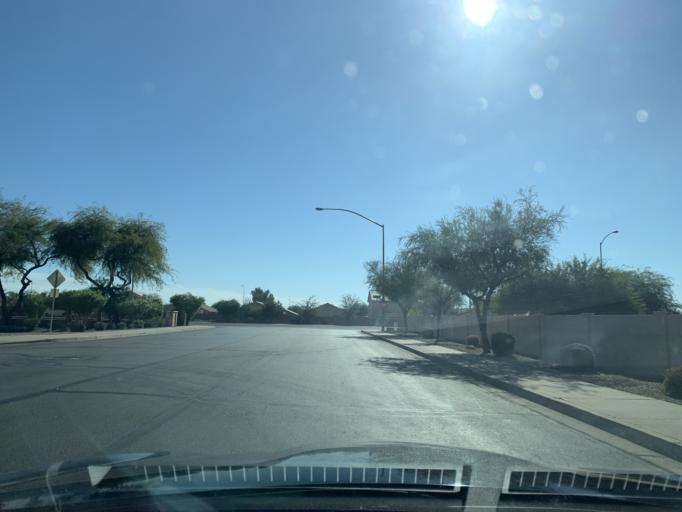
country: US
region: Arizona
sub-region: Pinal County
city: Apache Junction
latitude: 33.3798
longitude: -111.6242
